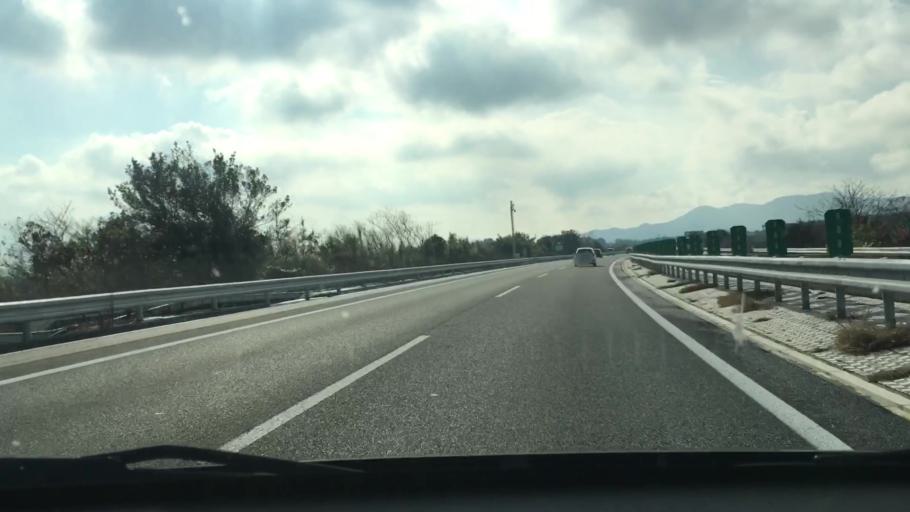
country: JP
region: Kumamoto
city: Uto
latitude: 32.7154
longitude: 130.7668
